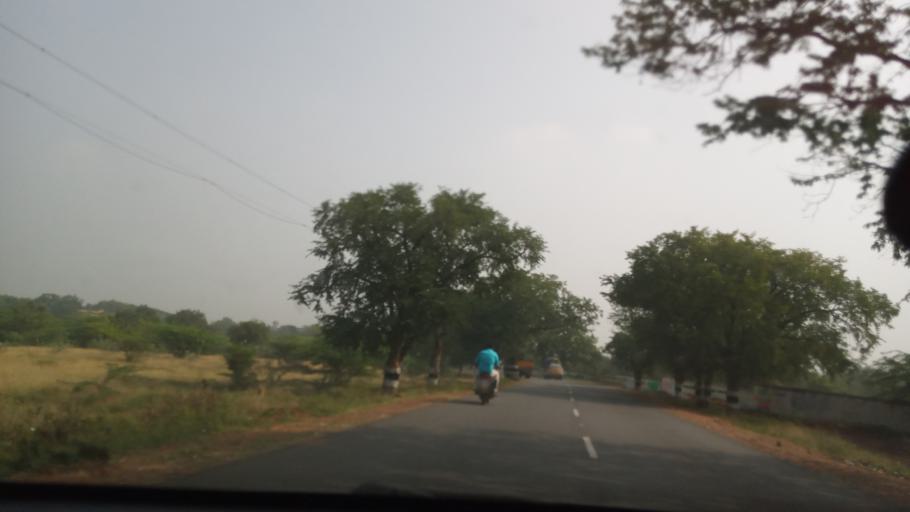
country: IN
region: Tamil Nadu
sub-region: Erode
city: Punjai Puliyampatti
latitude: 11.4289
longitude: 77.1981
